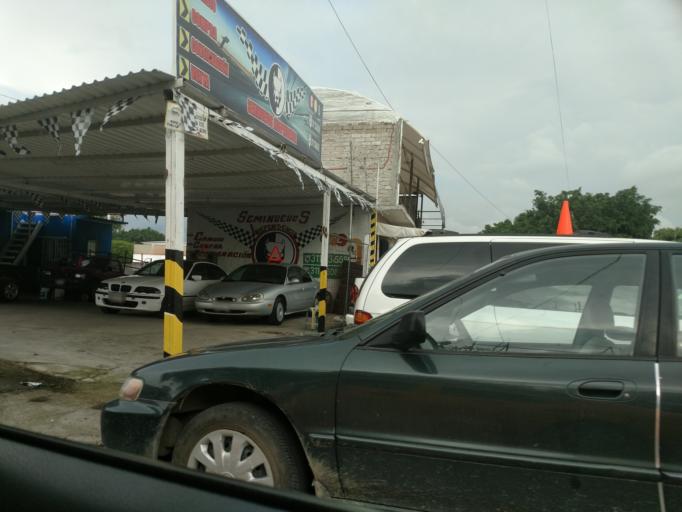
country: MX
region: Nayarit
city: Tepic
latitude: 21.4838
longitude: -104.8833
